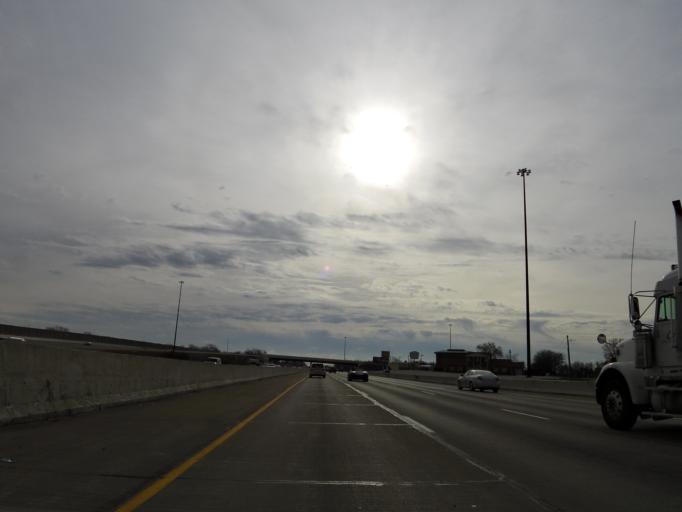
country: US
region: Indiana
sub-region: Marion County
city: Lawrence
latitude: 39.8499
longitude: -86.0460
